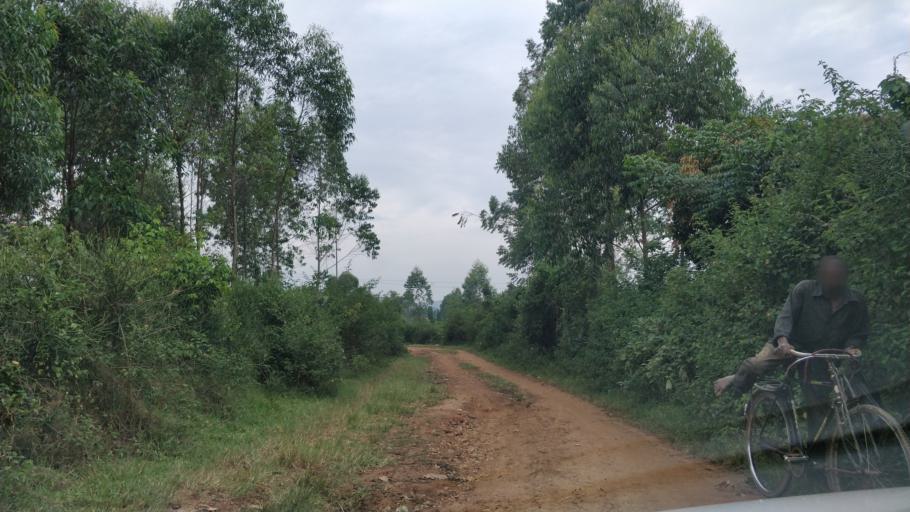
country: UG
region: Western Region
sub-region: Sheema District
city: Kibingo
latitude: -0.6942
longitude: 30.3900
